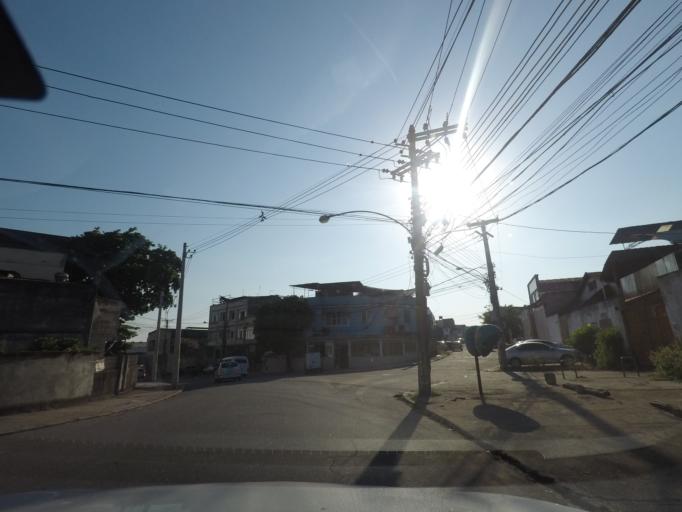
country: BR
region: Rio de Janeiro
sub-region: Rio De Janeiro
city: Rio de Janeiro
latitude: -22.8454
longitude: -43.2506
